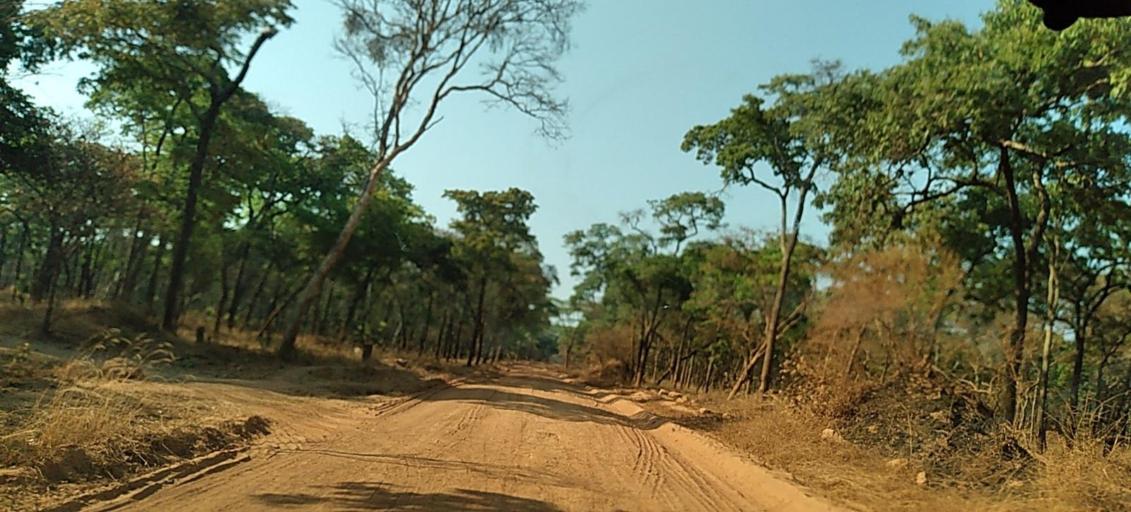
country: ZM
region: North-Western
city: Kasempa
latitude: -13.6101
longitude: 25.9783
